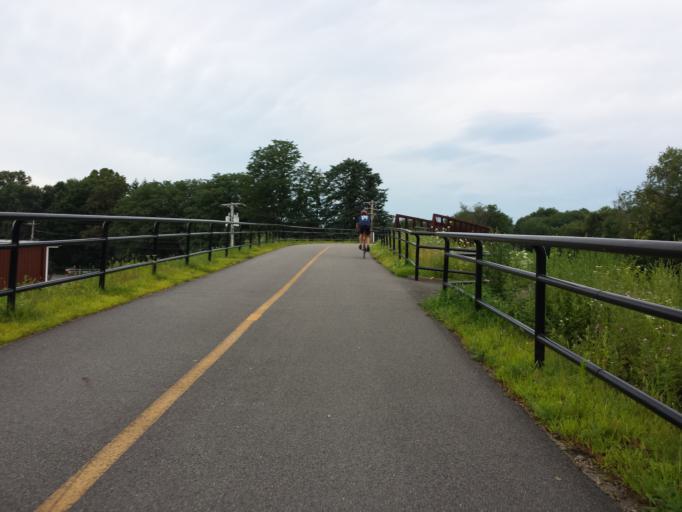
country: US
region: New York
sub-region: Dutchess County
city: Myers Corner
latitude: 41.6069
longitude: -73.8394
